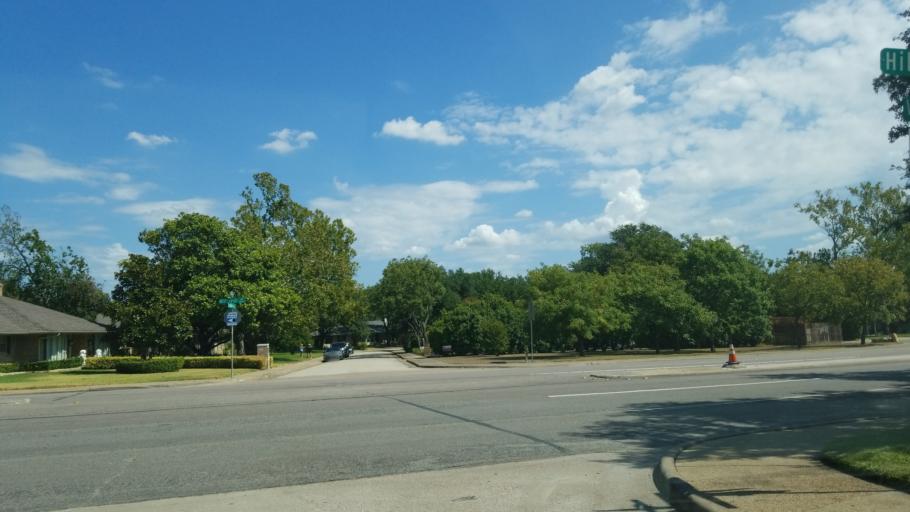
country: US
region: Texas
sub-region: Dallas County
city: Addison
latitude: 32.9537
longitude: -96.7869
